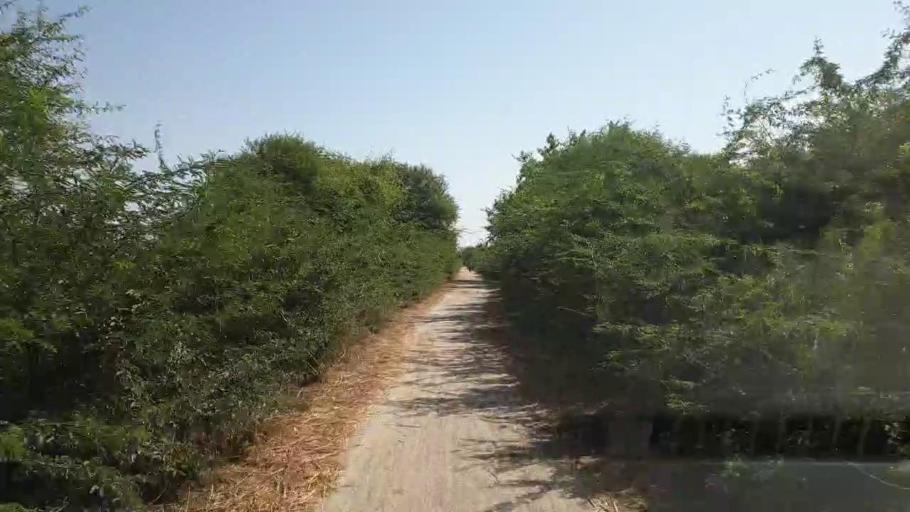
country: PK
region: Sindh
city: Tando Bago
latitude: 24.6516
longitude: 68.9831
